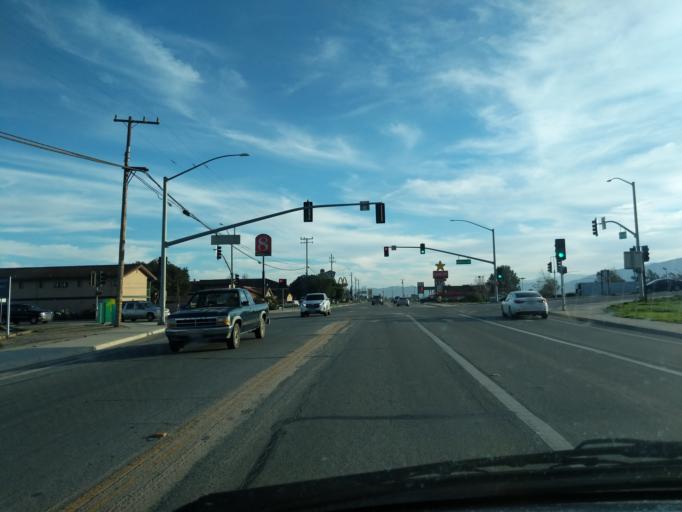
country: US
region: California
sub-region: Monterey County
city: Soledad
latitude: 36.4208
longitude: -121.3229
